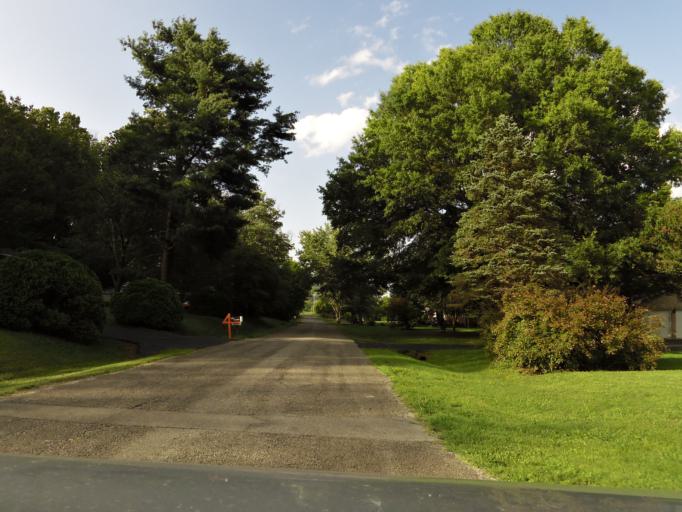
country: US
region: Tennessee
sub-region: Blount County
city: Eagleton Village
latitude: 35.8088
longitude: -83.9344
